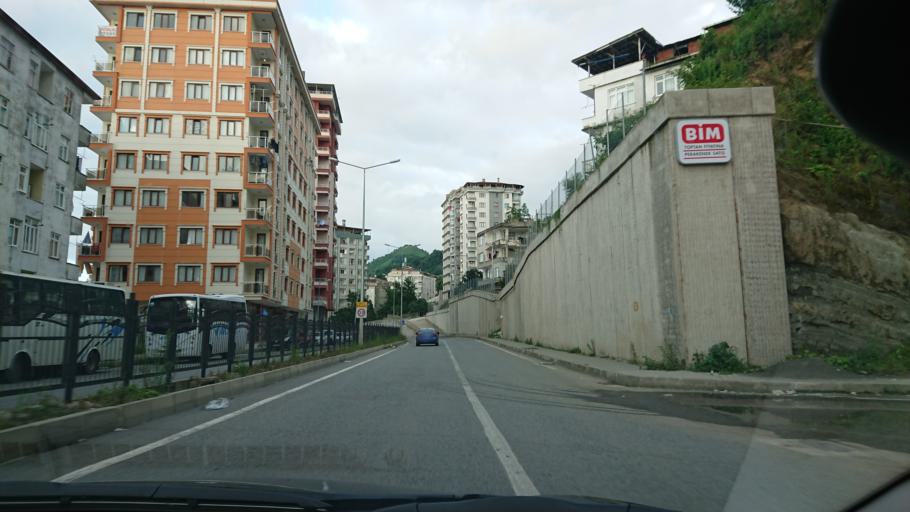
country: TR
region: Rize
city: Rize
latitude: 41.0209
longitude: 40.5313
